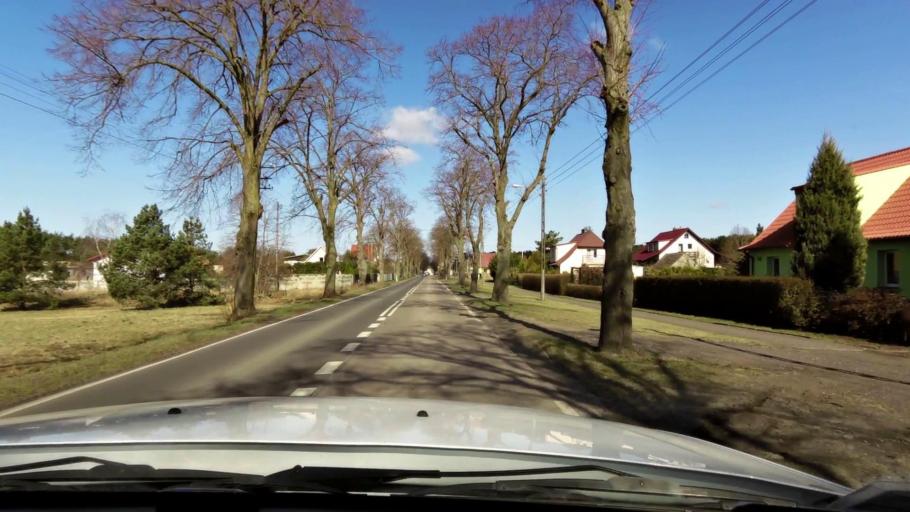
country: PL
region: West Pomeranian Voivodeship
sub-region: Powiat gryfinski
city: Gryfino
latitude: 53.2188
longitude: 14.4925
